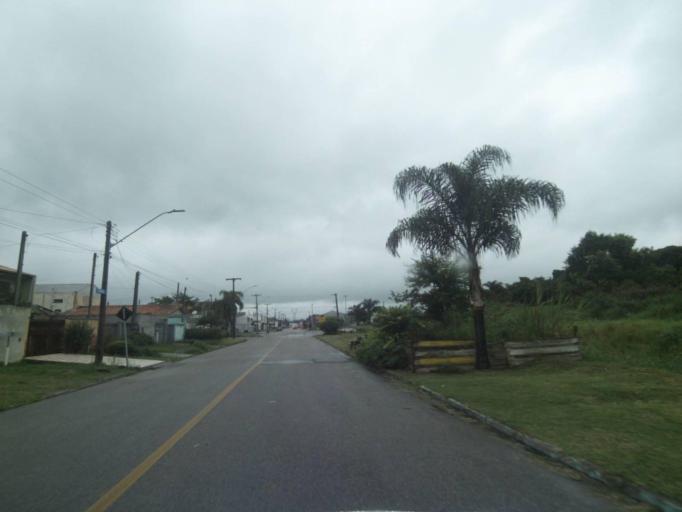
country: BR
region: Parana
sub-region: Araucaria
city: Araucaria
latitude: -25.5392
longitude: -49.3418
